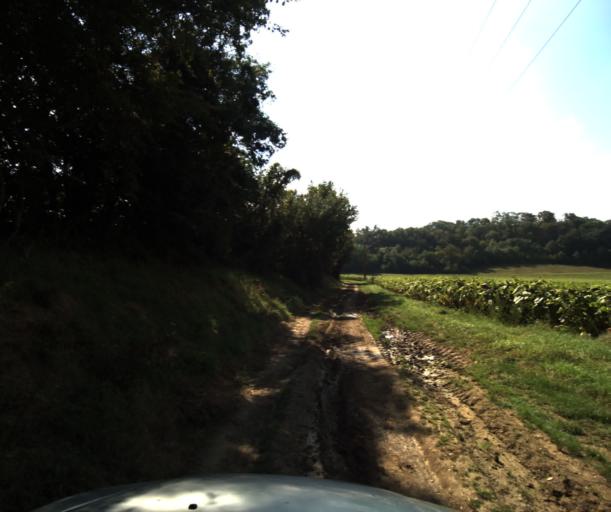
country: FR
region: Midi-Pyrenees
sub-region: Departement de la Haute-Garonne
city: Portet-sur-Garonne
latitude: 43.5184
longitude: 1.4222
